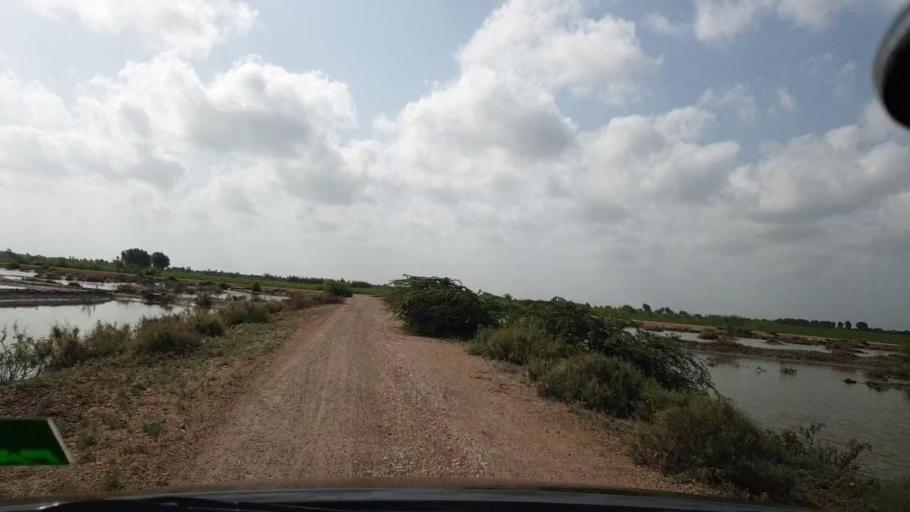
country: PK
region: Sindh
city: Kadhan
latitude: 24.6345
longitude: 69.0894
